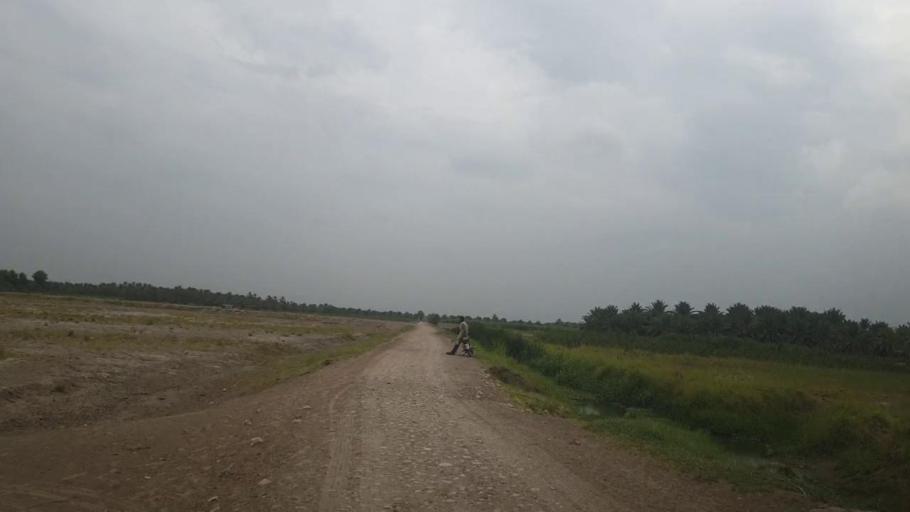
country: PK
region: Sindh
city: Khairpur
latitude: 27.5628
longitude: 68.7129
